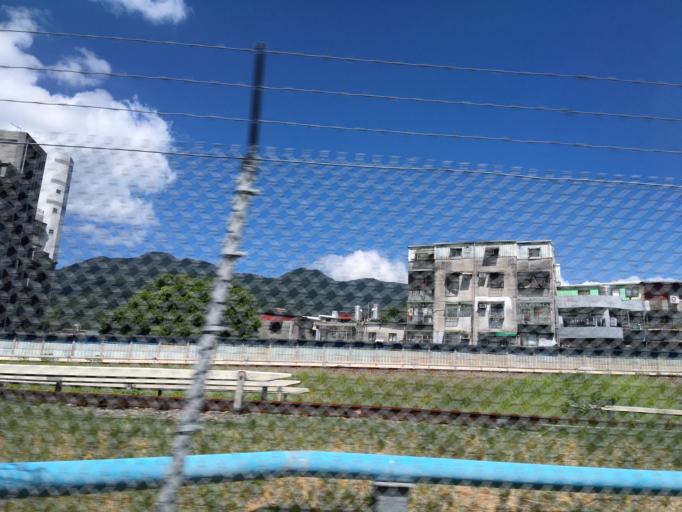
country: TW
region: Taipei
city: Taipei
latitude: 25.1368
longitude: 121.4927
